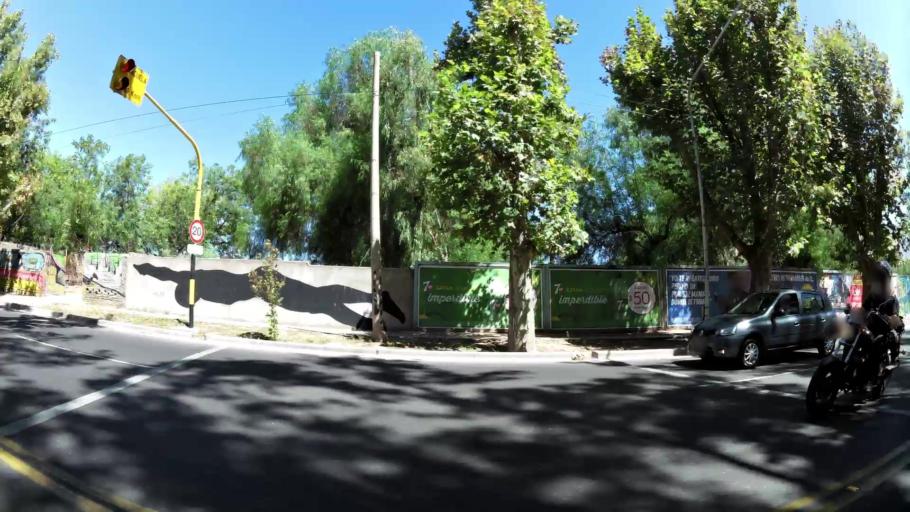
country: AR
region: Mendoza
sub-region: Departamento de Godoy Cruz
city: Godoy Cruz
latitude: -32.9085
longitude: -68.8656
